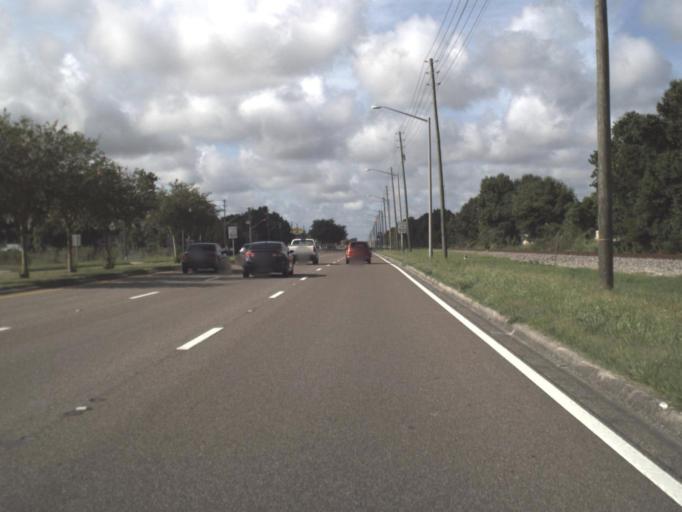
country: US
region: Florida
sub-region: Pasco County
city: Land O' Lakes
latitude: 28.2085
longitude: -82.4623
